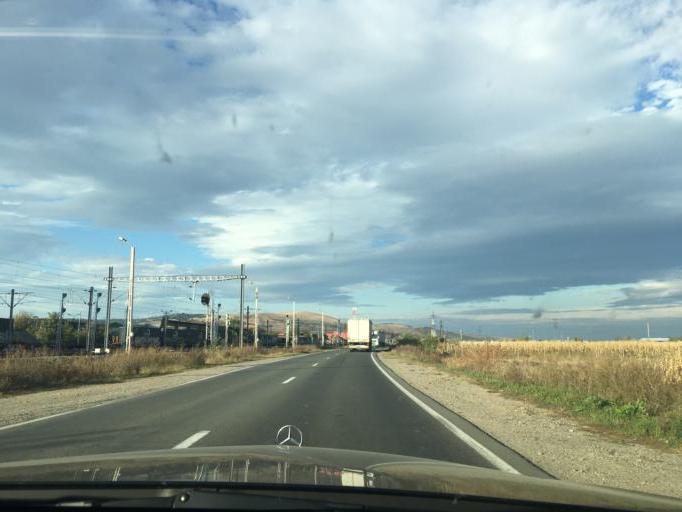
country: RO
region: Alba
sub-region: Municipiul Alba Iulia
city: Barabant
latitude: 46.0867
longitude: 23.5978
